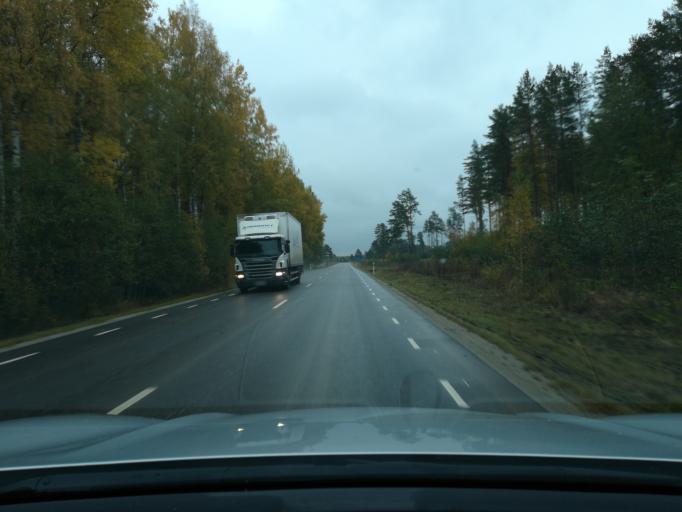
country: EE
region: Ida-Virumaa
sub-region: Johvi vald
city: Johvi
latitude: 59.2970
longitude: 27.4836
